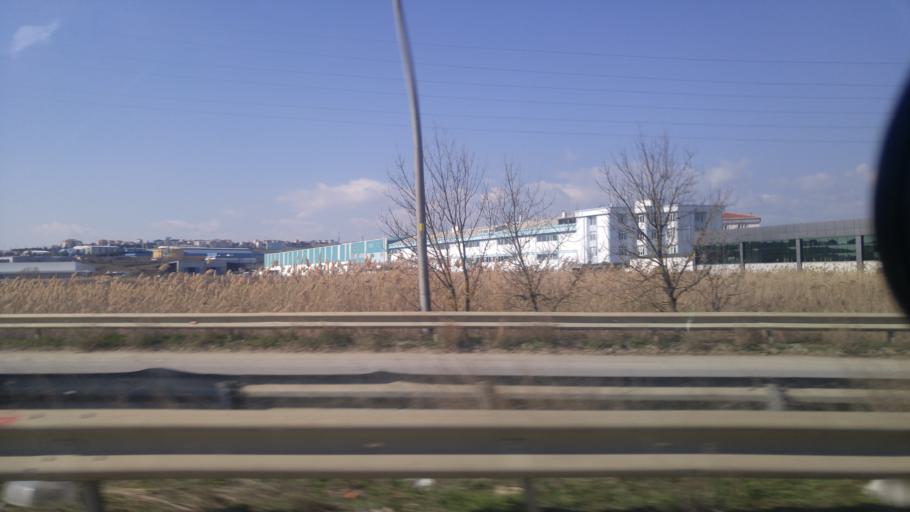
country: TR
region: Istanbul
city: Canta
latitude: 41.0715
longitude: 28.1038
